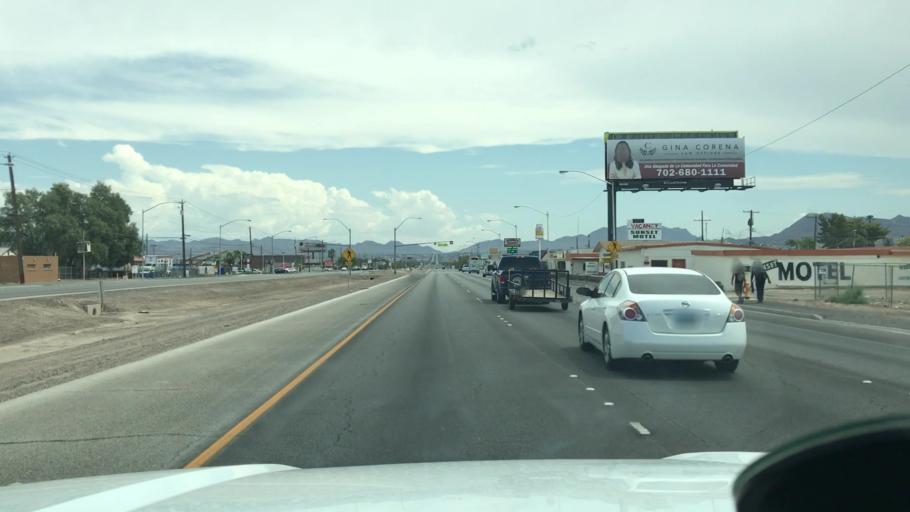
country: US
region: Nevada
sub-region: Clark County
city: Whitney
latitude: 36.0934
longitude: -115.0429
